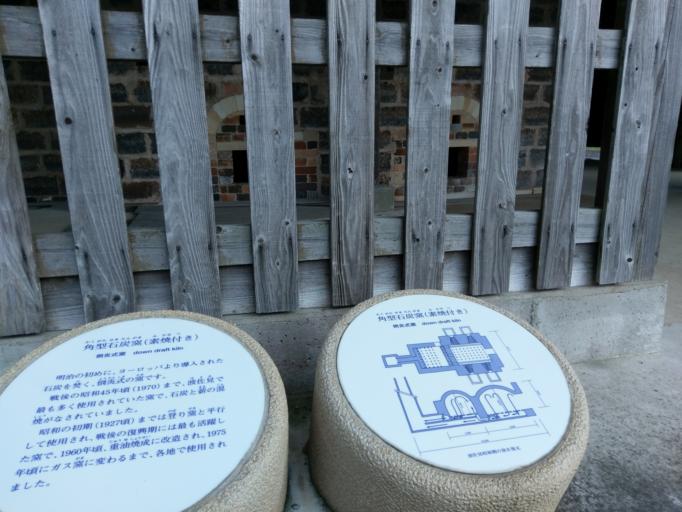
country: JP
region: Saga Prefecture
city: Ureshinomachi-shimojuku
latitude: 33.1412
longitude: 129.9109
